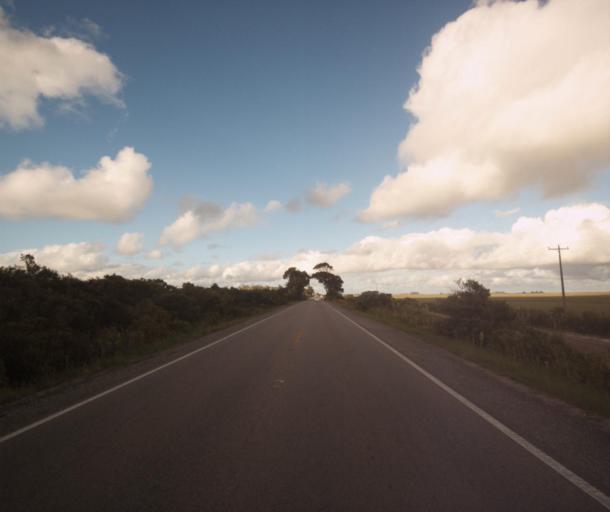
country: BR
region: Rio Grande do Sul
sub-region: Rio Grande
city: Rio Grande
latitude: -32.1896
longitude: -52.4325
